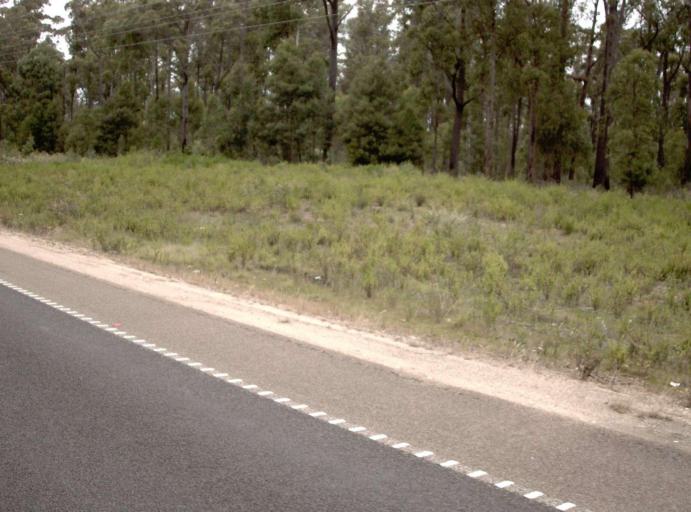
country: AU
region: Victoria
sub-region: East Gippsland
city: Lakes Entrance
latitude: -37.7162
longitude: 148.0762
